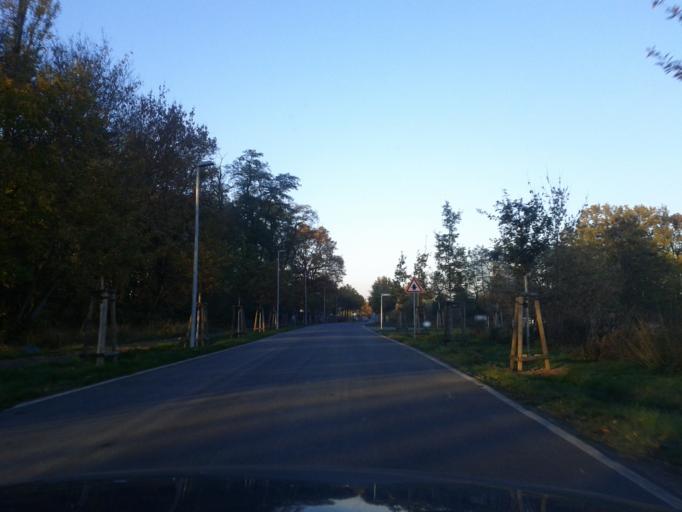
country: DE
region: Brandenburg
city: Schoneiche
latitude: 52.4928
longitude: 13.7023
